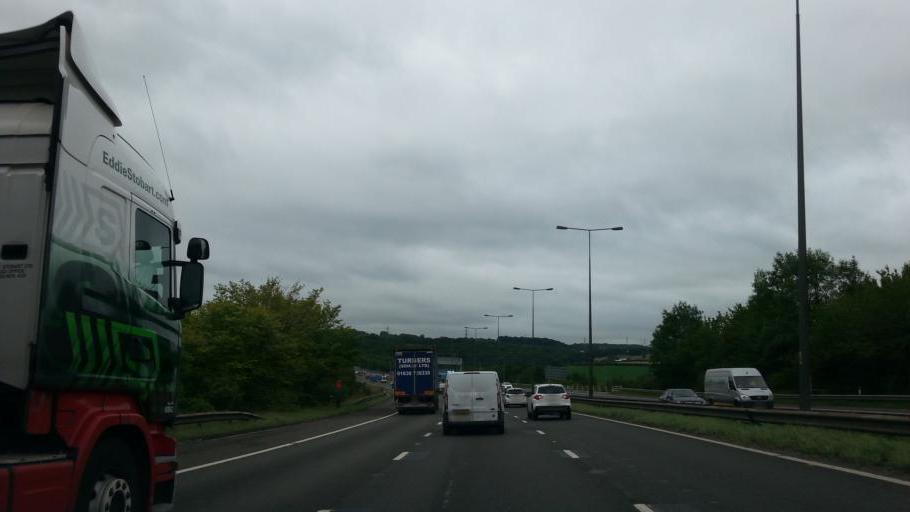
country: GB
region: England
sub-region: Calderdale
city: Brighouse
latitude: 53.6957
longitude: -1.7527
